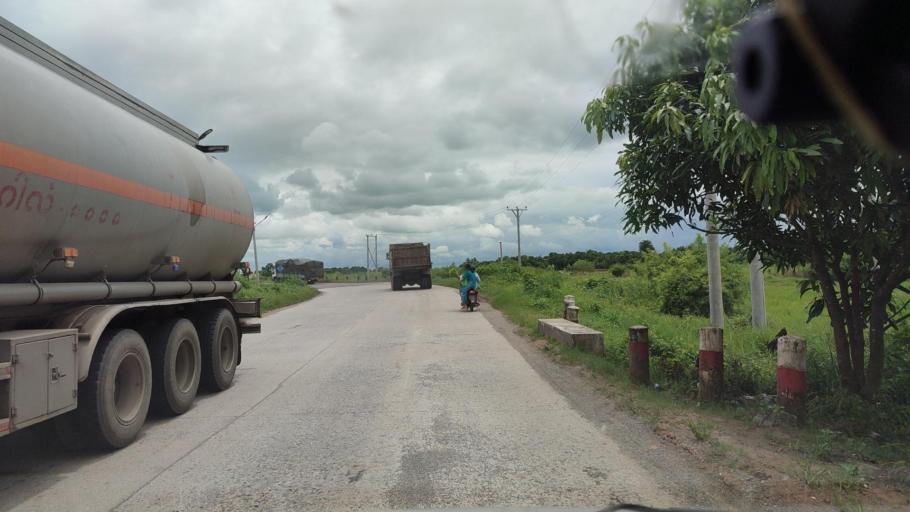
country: MM
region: Bago
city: Bago
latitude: 17.3782
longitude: 96.4775
